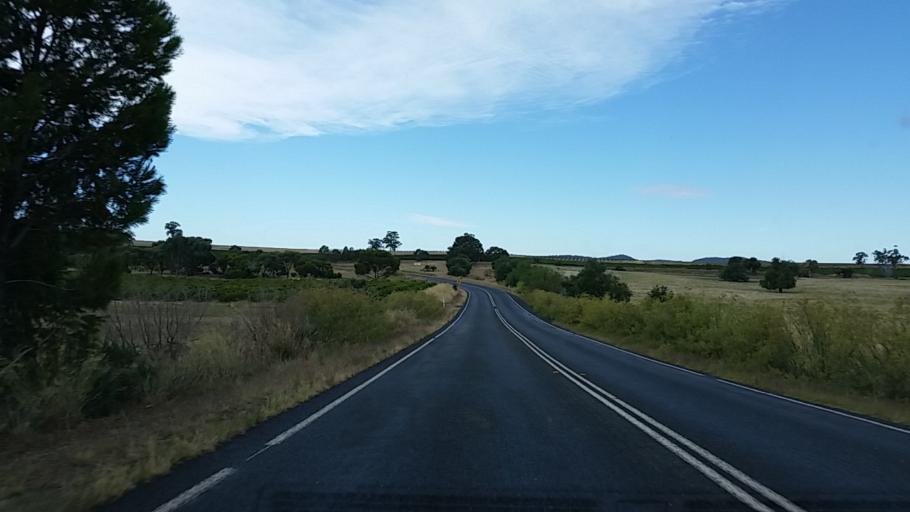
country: AU
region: South Australia
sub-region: Barossa
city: Tanunda
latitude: -34.5381
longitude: 138.9250
